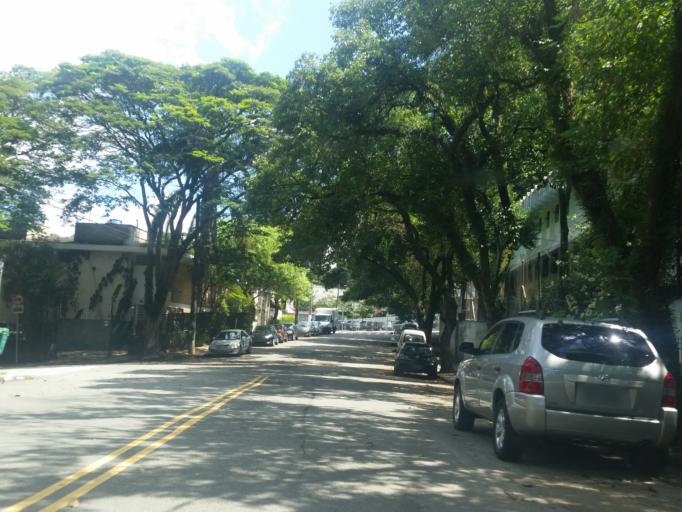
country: BR
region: Sao Paulo
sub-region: Sao Paulo
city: Sao Paulo
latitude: -23.5505
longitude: -46.6829
